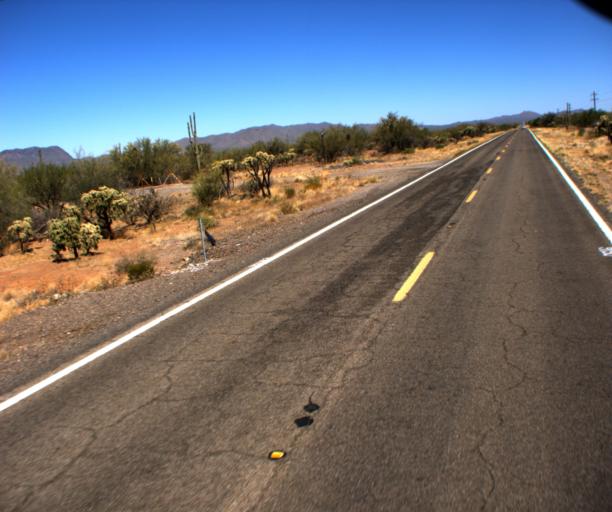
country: US
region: Arizona
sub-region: Pima County
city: Sells
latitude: 32.0493
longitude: -112.0247
